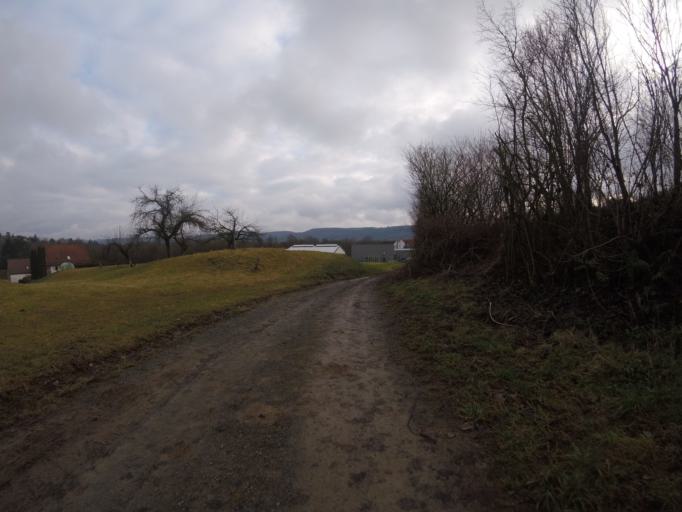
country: DE
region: Baden-Wuerttemberg
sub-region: Regierungsbezirk Stuttgart
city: Allmersbach im Tal
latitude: 48.9225
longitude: 9.4818
